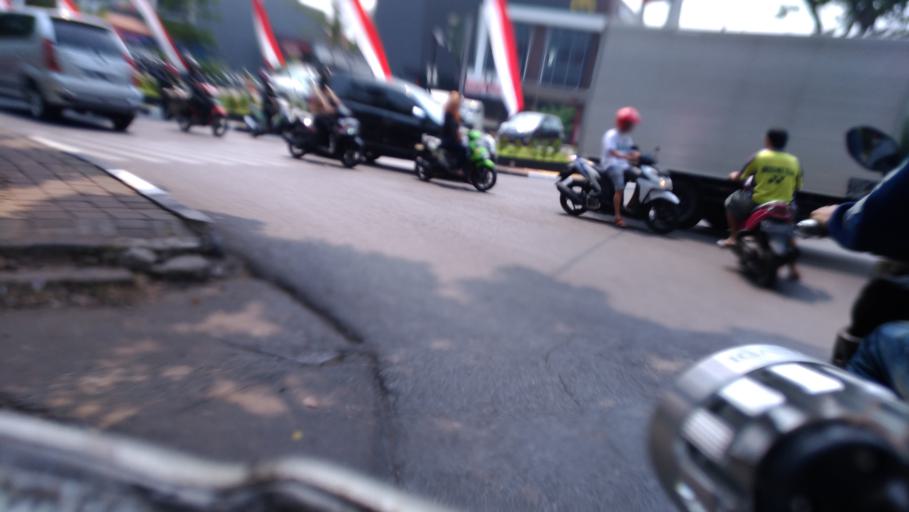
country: ID
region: West Java
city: Cileungsir
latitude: -6.3317
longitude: 106.8880
